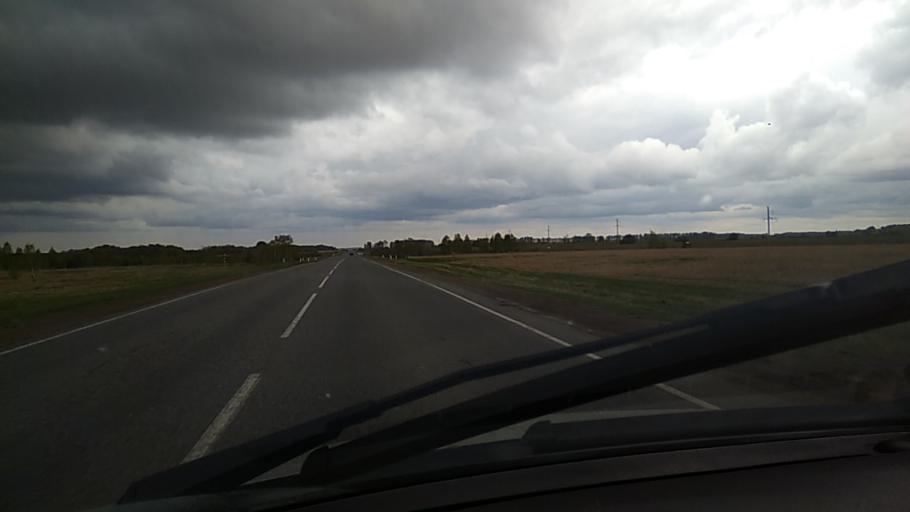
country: RU
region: Kurgan
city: Dalmatovo
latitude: 56.2897
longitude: 62.8491
